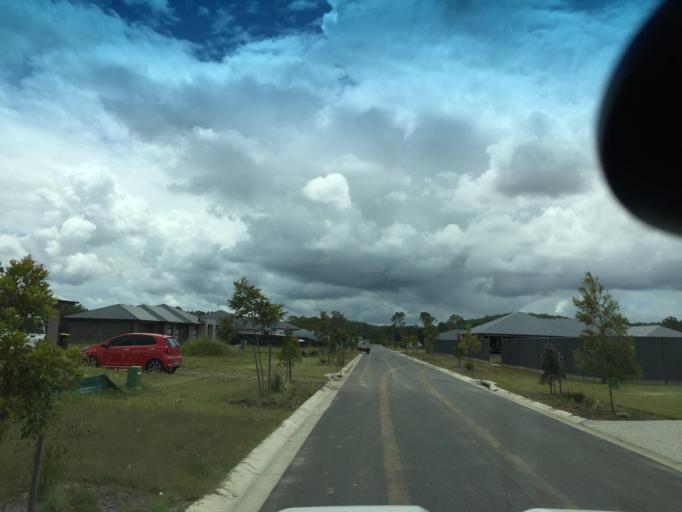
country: AU
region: Queensland
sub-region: Moreton Bay
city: Caboolture
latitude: -27.0431
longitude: 152.9260
